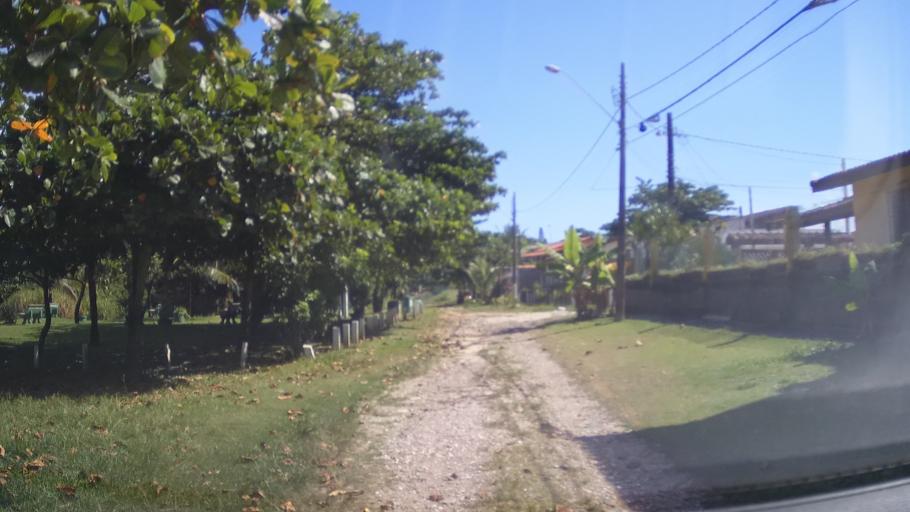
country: BR
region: Sao Paulo
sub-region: Itanhaem
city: Itanhaem
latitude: -24.1614
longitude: -46.7424
